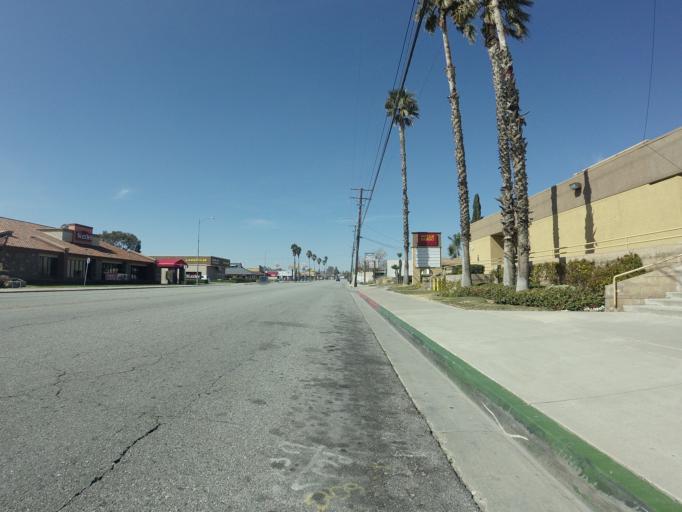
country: US
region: California
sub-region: Riverside County
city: Banning
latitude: 33.9255
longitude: -116.8955
